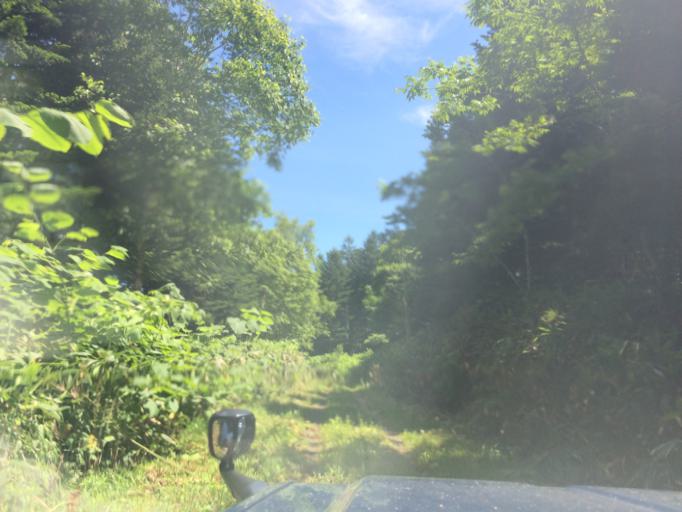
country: JP
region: Hokkaido
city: Niseko Town
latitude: 42.8621
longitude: 140.8178
